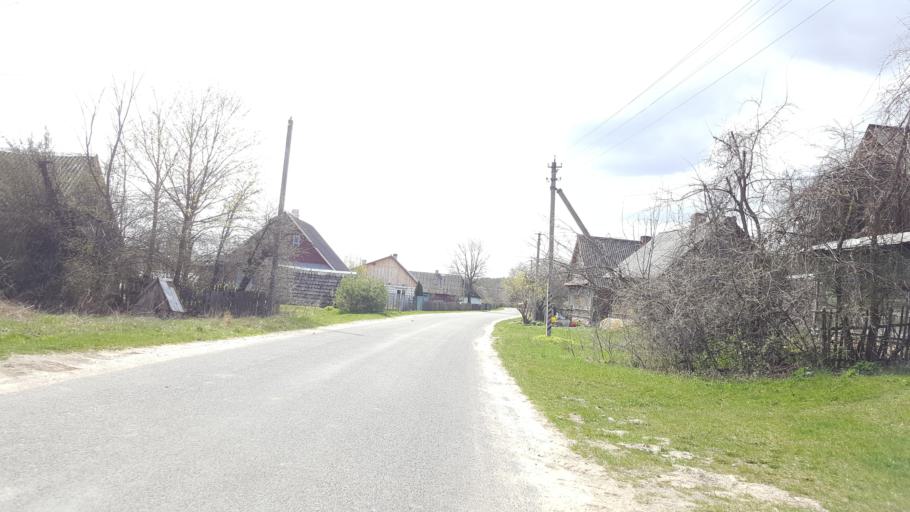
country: BY
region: Brest
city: Kamyanyets
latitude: 52.3784
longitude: 23.7400
